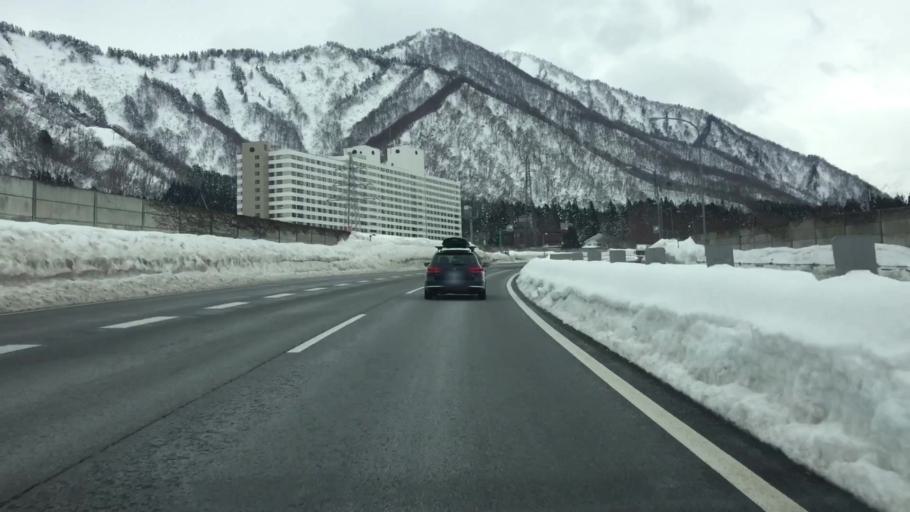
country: JP
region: Niigata
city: Shiozawa
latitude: 36.9065
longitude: 138.8452
